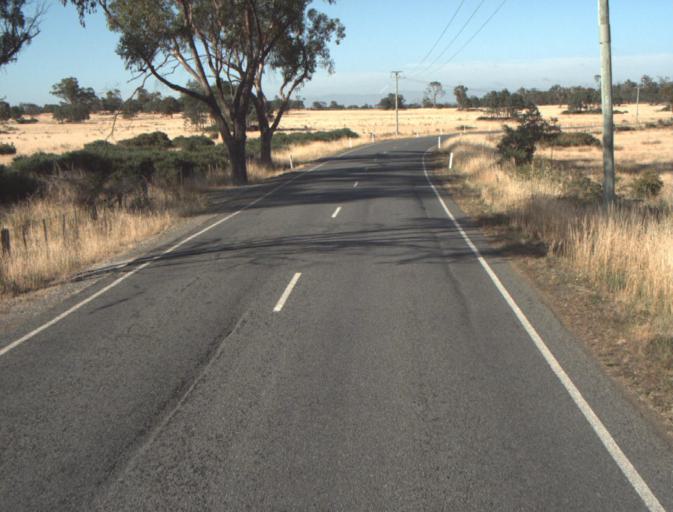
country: AU
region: Tasmania
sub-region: Launceston
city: Newstead
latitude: -41.4445
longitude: 147.2524
